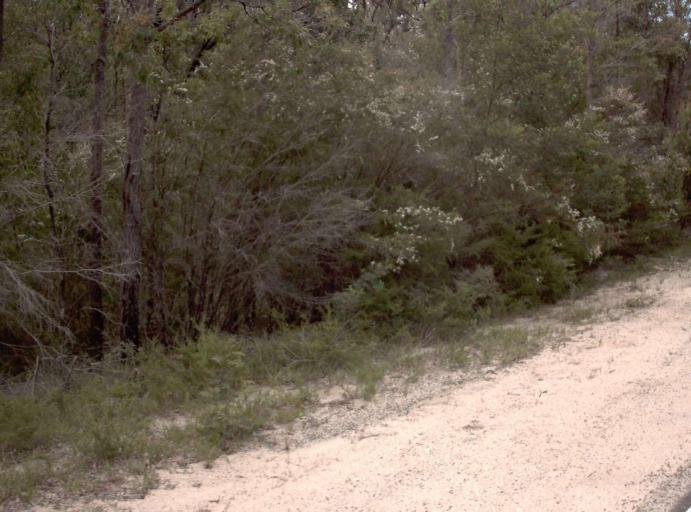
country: AU
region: New South Wales
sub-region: Bega Valley
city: Eden
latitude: -37.4164
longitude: 149.6527
